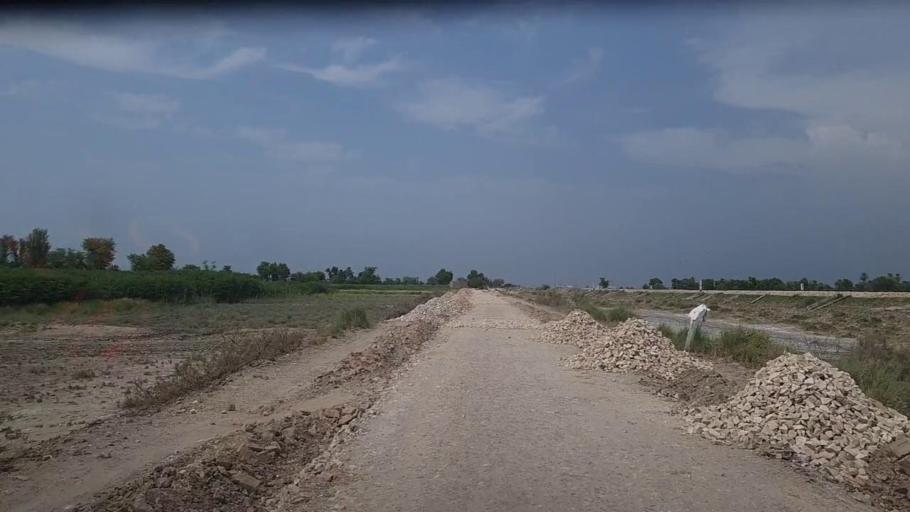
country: PK
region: Sindh
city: Bhiria
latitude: 26.9177
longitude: 68.2959
